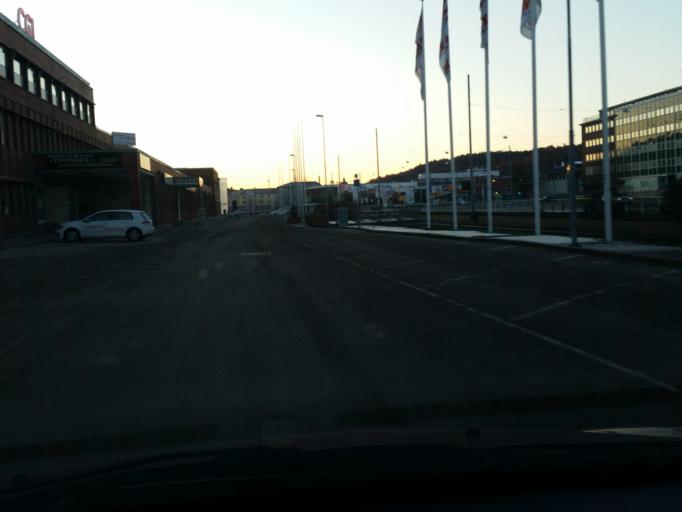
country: SE
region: Vaestra Goetaland
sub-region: Molndal
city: Moelndal
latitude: 57.6799
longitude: 12.0038
